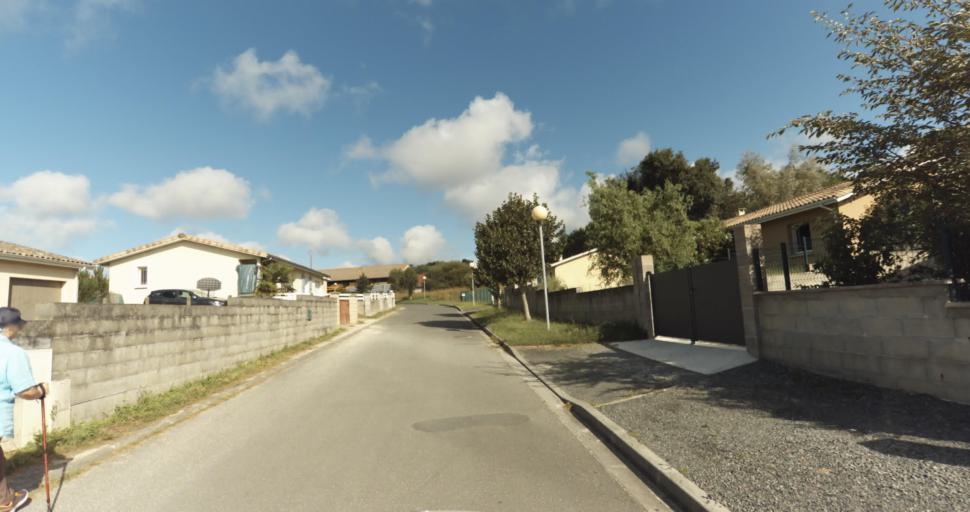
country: FR
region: Aquitaine
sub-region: Departement de la Gironde
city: Bazas
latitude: 44.4387
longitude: -0.2421
